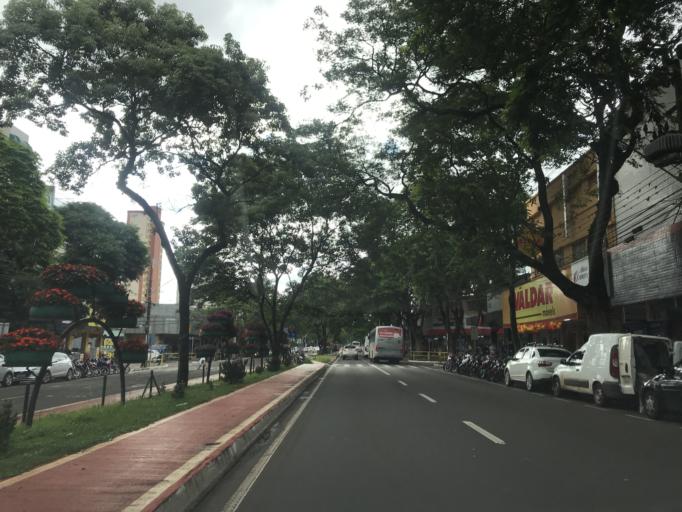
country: BR
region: Parana
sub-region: Maringa
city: Maringa
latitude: -23.4209
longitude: -51.9340
